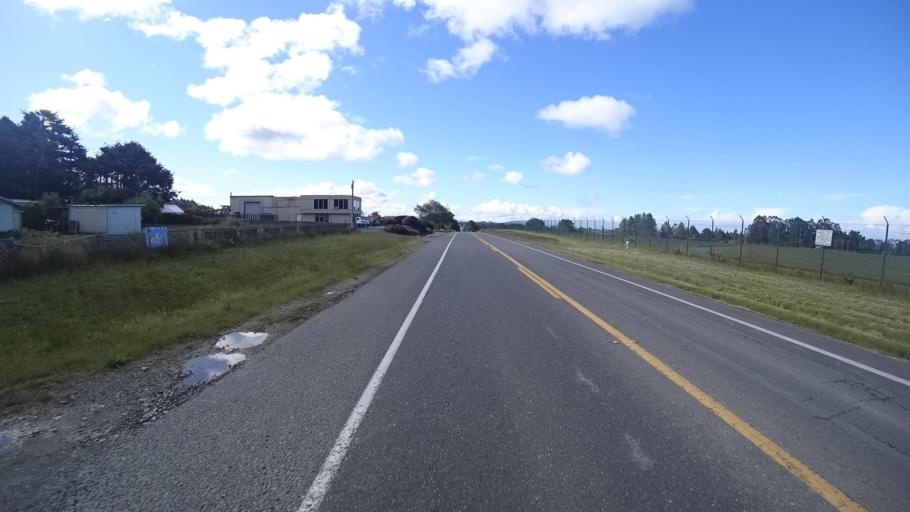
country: US
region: California
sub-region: Humboldt County
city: McKinleyville
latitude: 40.9692
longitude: -124.1006
